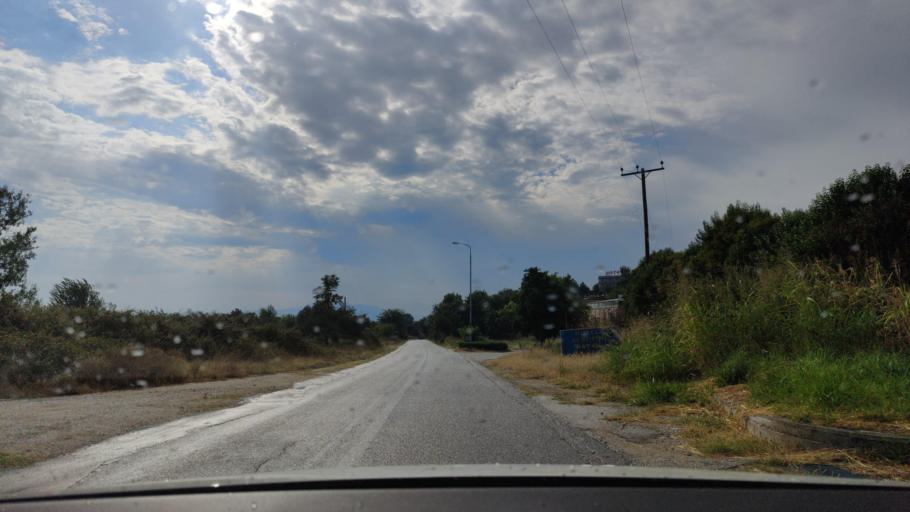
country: GR
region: Central Macedonia
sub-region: Nomos Serron
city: Lefkonas
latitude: 41.1033
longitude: 23.4818
